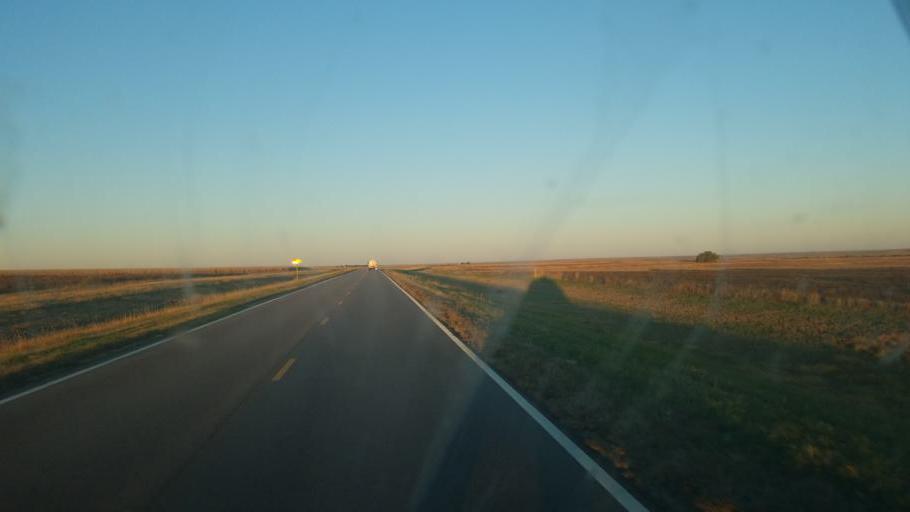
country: US
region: Kansas
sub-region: Wallace County
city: Sharon Springs
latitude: 38.9011
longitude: -101.8487
